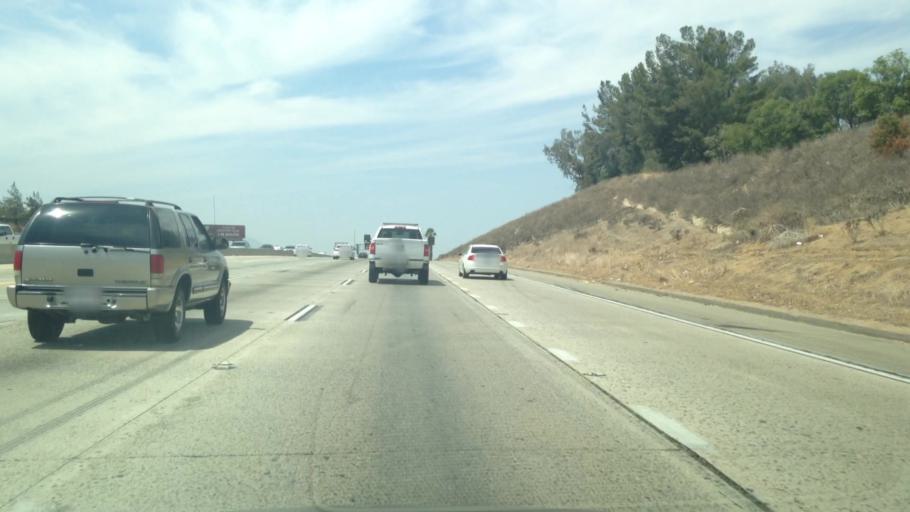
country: US
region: California
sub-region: Riverside County
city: Home Gardens
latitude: 33.8841
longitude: -117.5276
